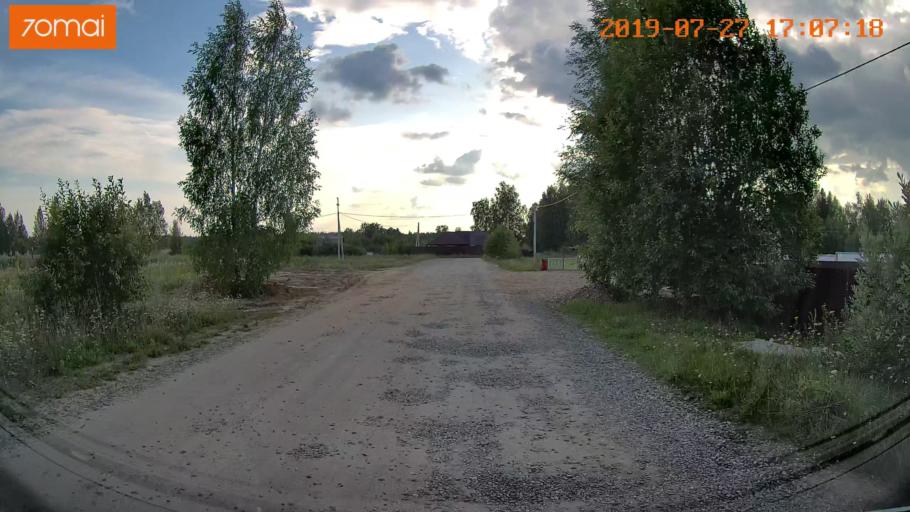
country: RU
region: Ivanovo
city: Novo-Talitsy
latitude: 57.0848
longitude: 40.8366
